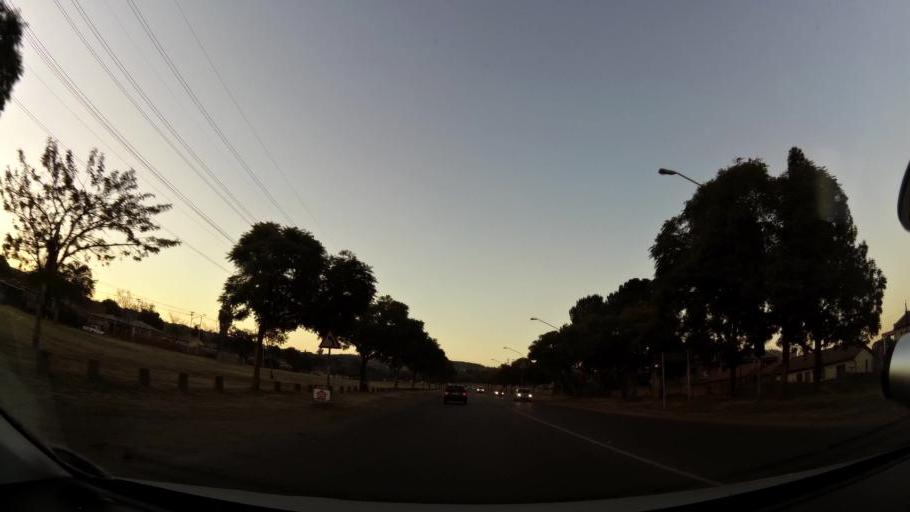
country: ZA
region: Gauteng
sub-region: City of Tshwane Metropolitan Municipality
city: Pretoria
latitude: -25.7396
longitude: 28.1361
